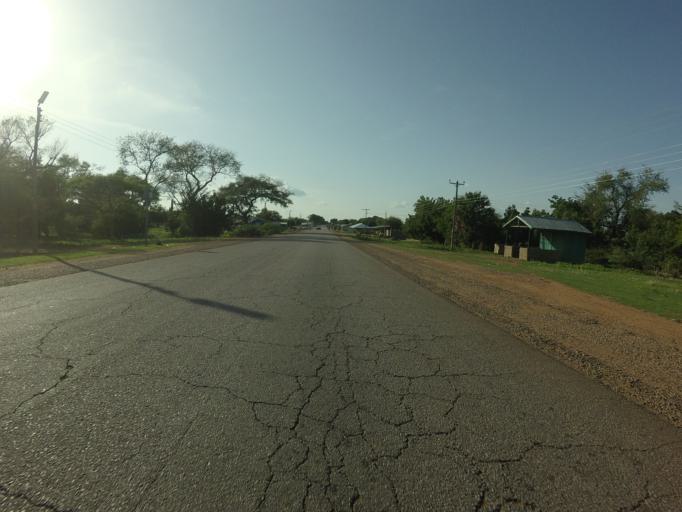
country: GH
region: Upper East
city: Navrongo
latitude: 10.9595
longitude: -1.0986
